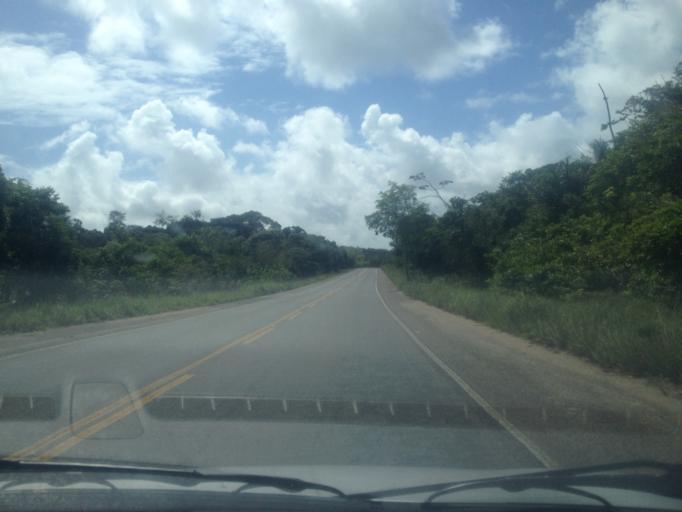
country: BR
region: Bahia
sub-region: Conde
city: Conde
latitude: -12.0389
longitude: -37.7057
